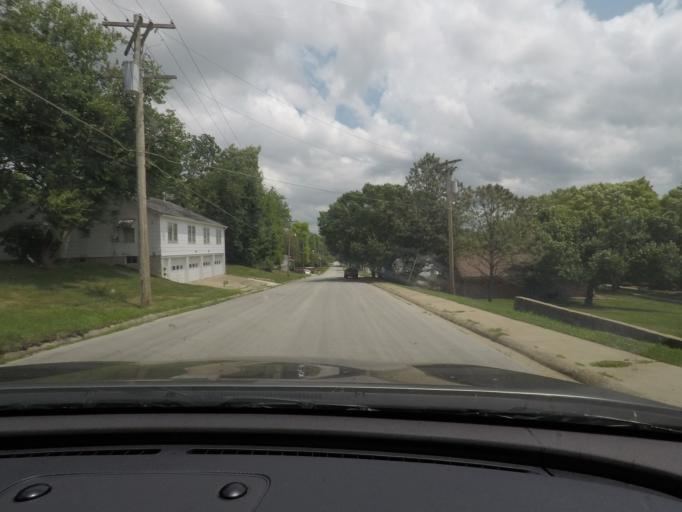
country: US
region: Missouri
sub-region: Carroll County
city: Carrollton
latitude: 39.3578
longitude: -93.4940
